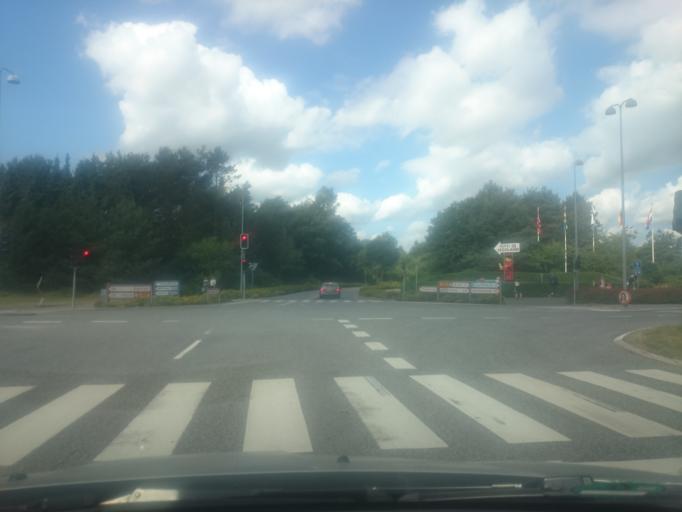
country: DK
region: South Denmark
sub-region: Billund Kommune
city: Billund
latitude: 55.7339
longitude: 9.1343
